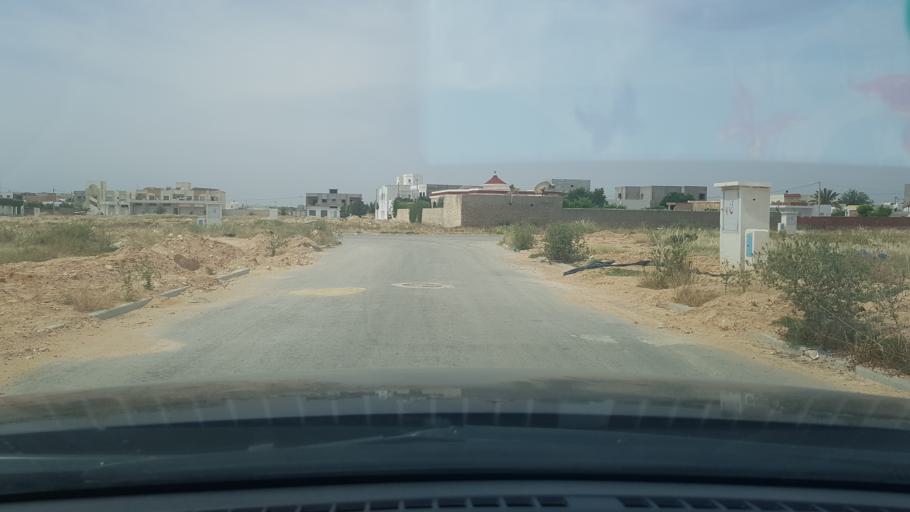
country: TN
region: Safaqis
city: Al Qarmadah
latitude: 34.8228
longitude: 10.7429
